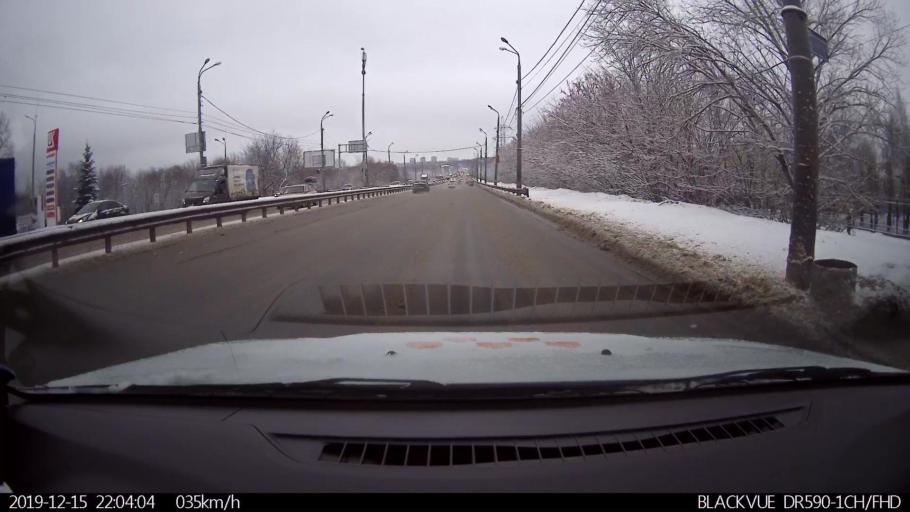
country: RU
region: Nizjnij Novgorod
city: Nizhniy Novgorod
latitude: 56.2583
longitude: 43.9325
